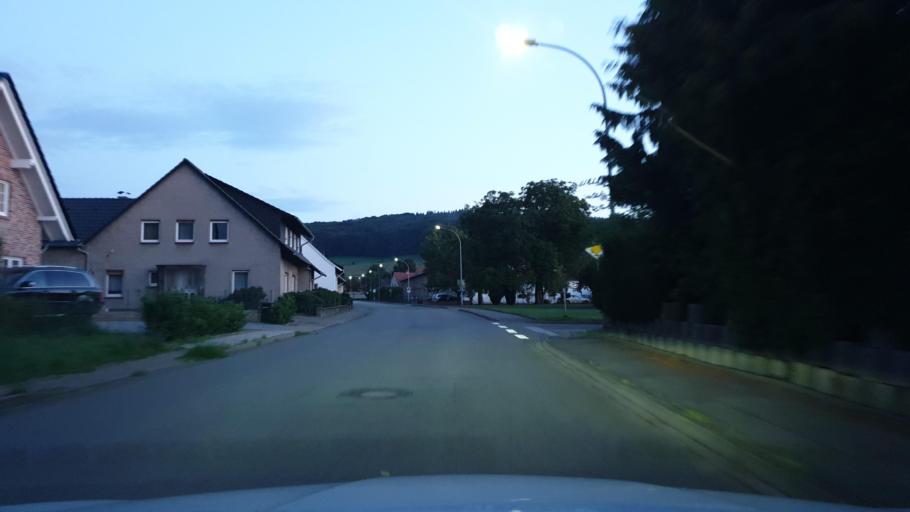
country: DE
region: North Rhine-Westphalia
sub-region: Regierungsbezirk Detmold
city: Huellhorst
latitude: 52.3130
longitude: 8.6669
